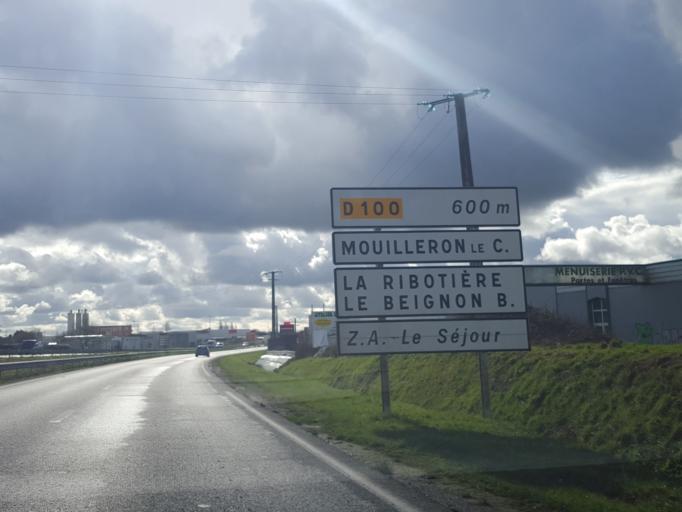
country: FR
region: Pays de la Loire
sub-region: Departement de la Vendee
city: Mouilleron-le-Captif
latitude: 46.7393
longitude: -1.4305
